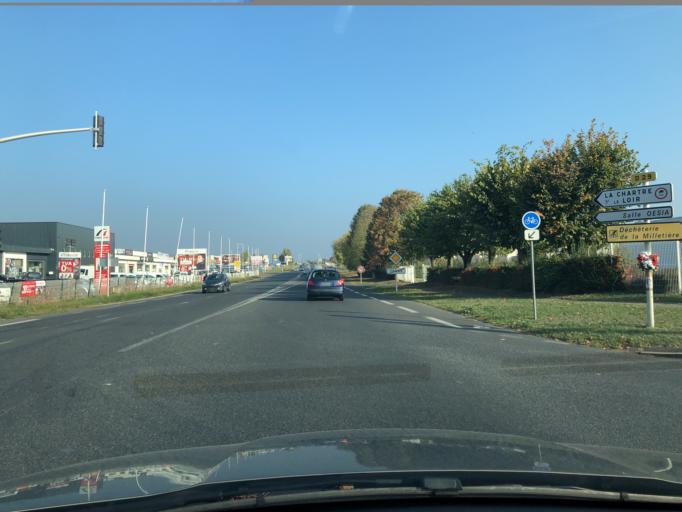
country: FR
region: Centre
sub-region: Departement d'Indre-et-Loire
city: Chanceaux-sur-Choisille
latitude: 47.4371
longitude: 0.6989
